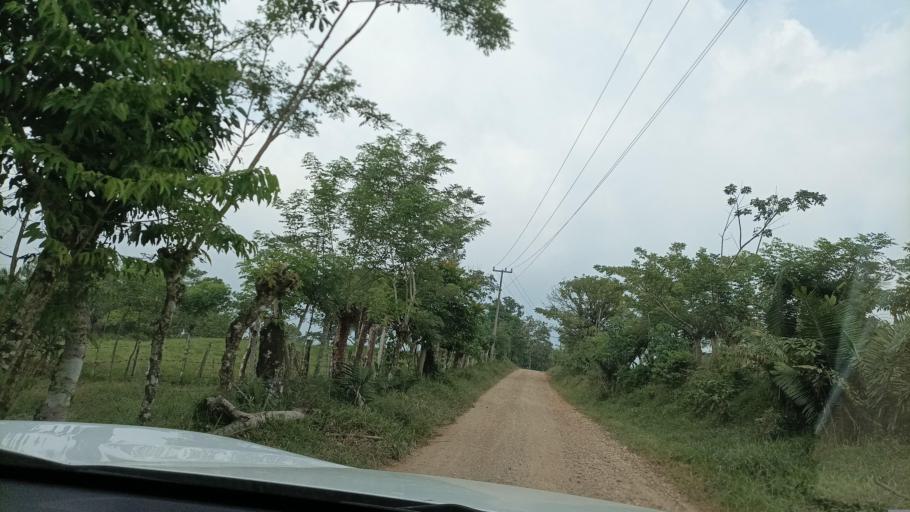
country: MX
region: Tabasco
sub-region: Huimanguillo
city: Francisco Rueda
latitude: 17.5905
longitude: -94.1992
